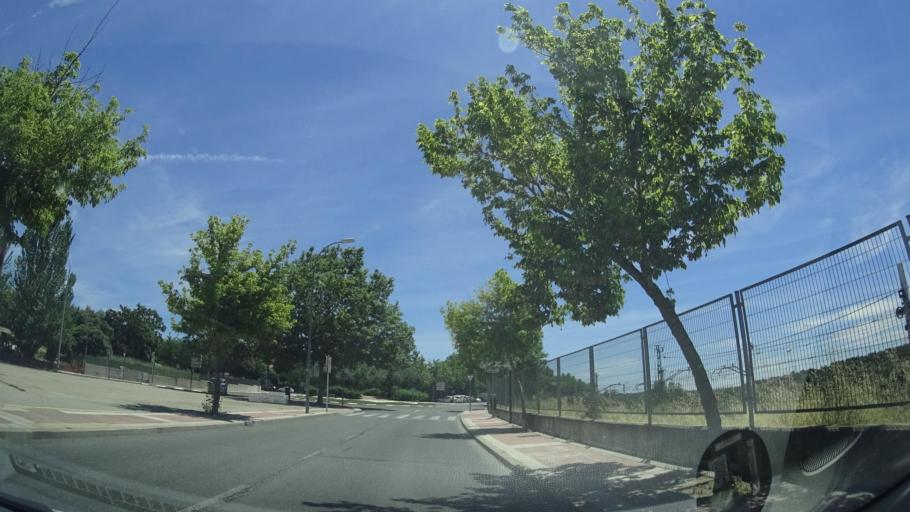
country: ES
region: Madrid
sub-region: Provincia de Madrid
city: Collado-Villalba
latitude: 40.6252
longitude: -4.0010
